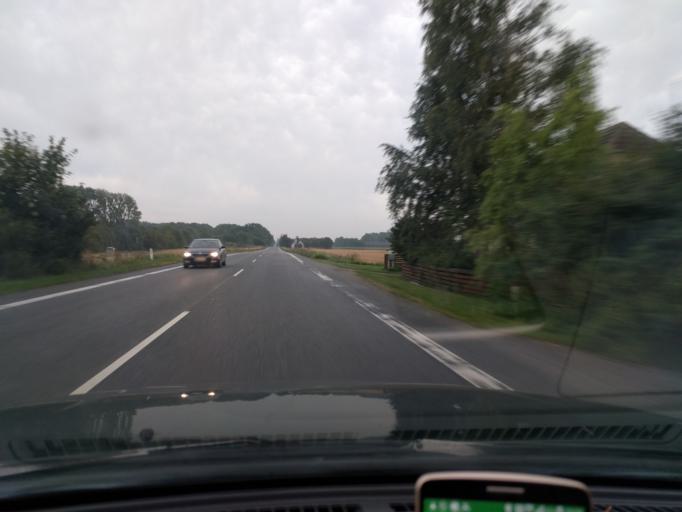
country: DK
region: Zealand
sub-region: Guldborgsund Kommune
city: Norre Alslev
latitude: 54.9310
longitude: 11.8712
